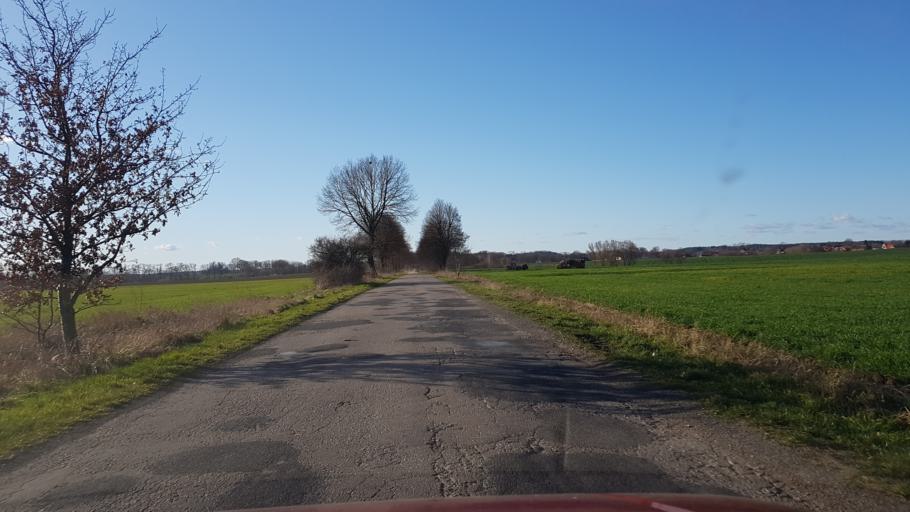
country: PL
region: West Pomeranian Voivodeship
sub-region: Powiat stargardzki
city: Stara Dabrowa
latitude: 53.3664
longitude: 15.1176
